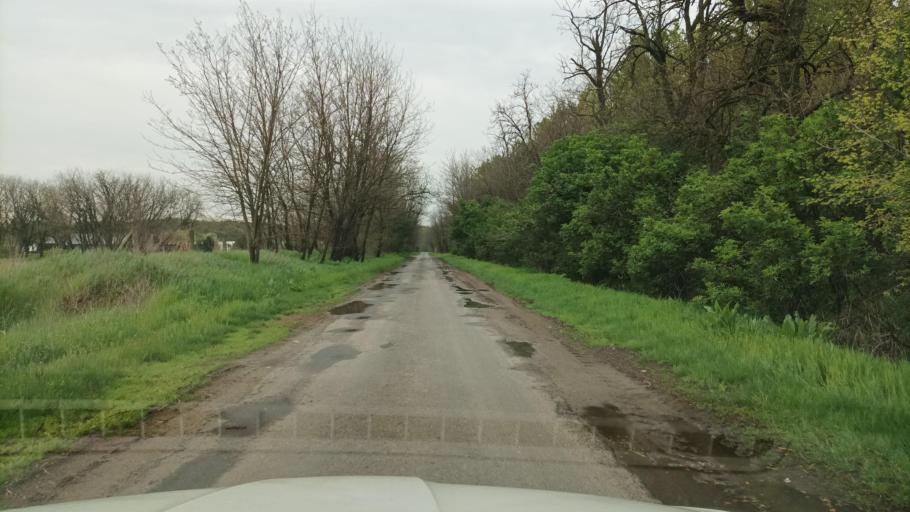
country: HU
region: Pest
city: Nagykoros
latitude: 46.9801
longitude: 19.8091
